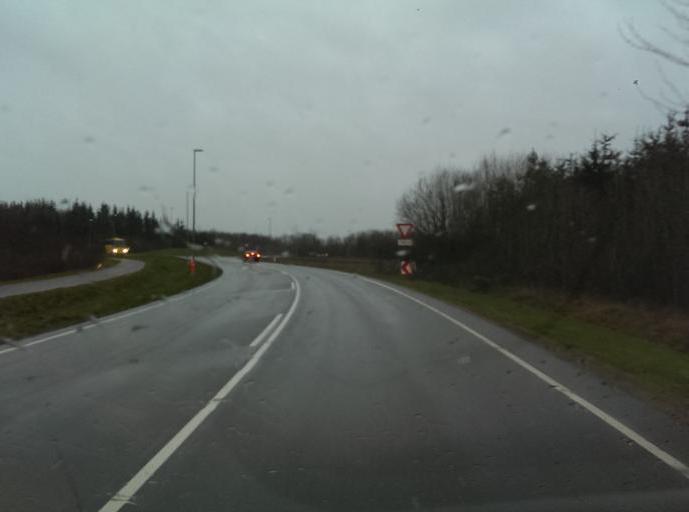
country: DK
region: South Denmark
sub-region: Esbjerg Kommune
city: Esbjerg
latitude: 55.4859
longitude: 8.5089
